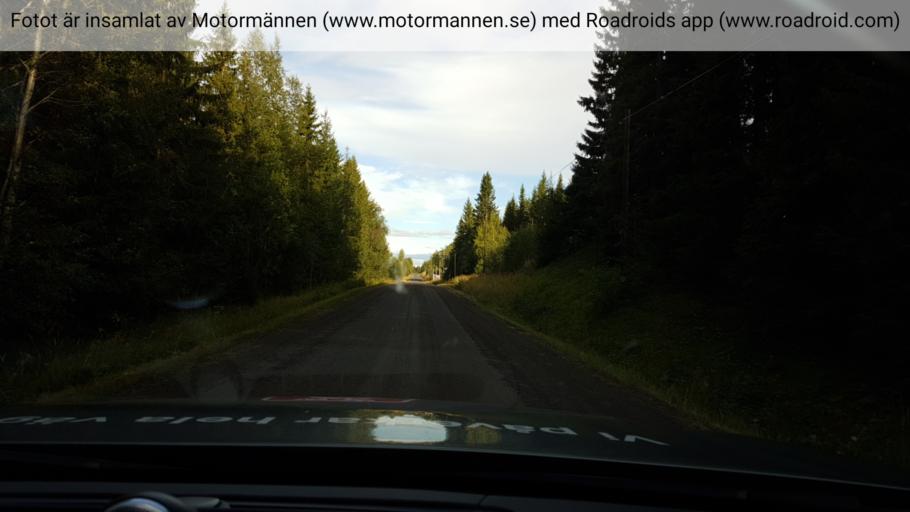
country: SE
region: Jaemtland
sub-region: Stroemsunds Kommun
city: Stroemsund
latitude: 64.1374
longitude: 15.7544
